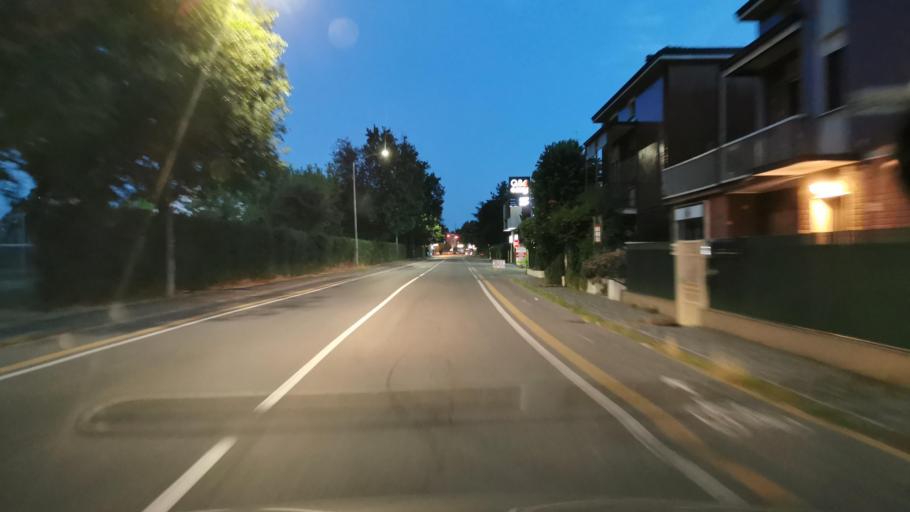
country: IT
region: Emilia-Romagna
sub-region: Provincia di Modena
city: Modena
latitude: 44.6292
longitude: 10.9269
